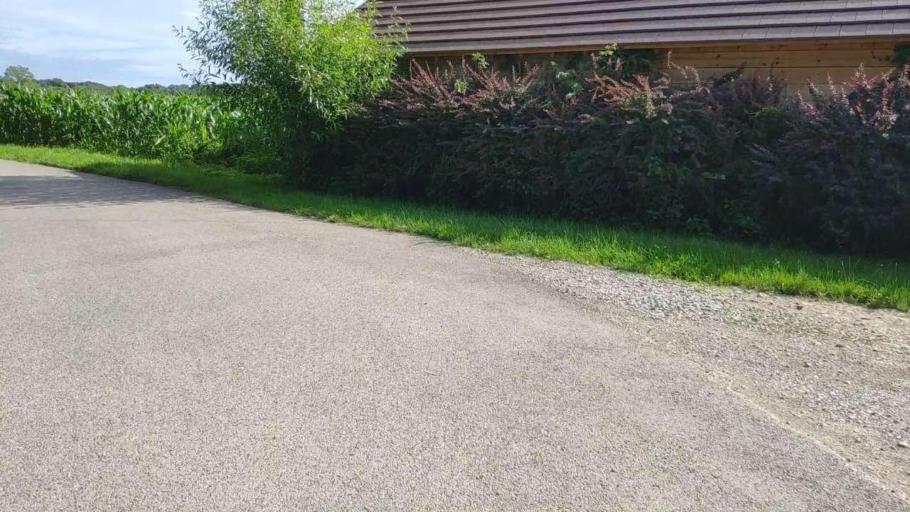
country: FR
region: Franche-Comte
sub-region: Departement du Jura
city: Bletterans
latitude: 46.8104
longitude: 5.5054
